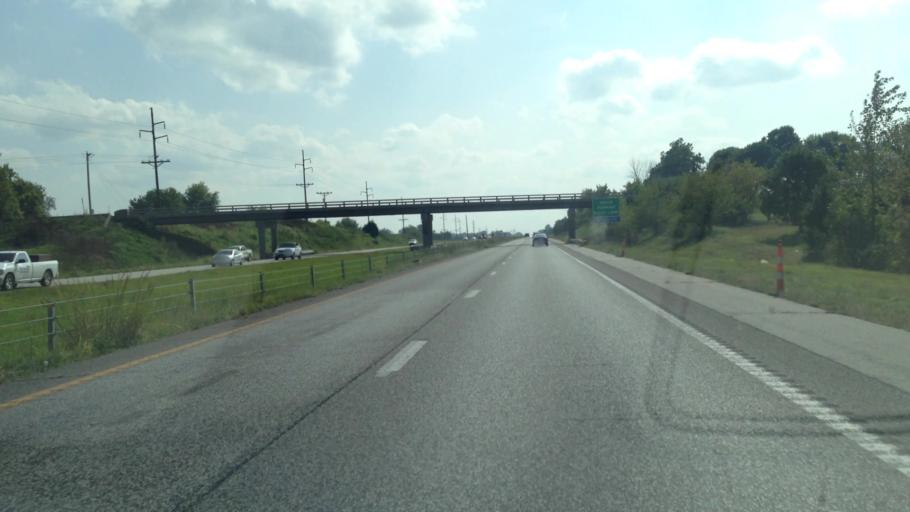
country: US
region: Missouri
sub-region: Clay County
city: Kearney
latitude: 39.3255
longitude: -94.3952
